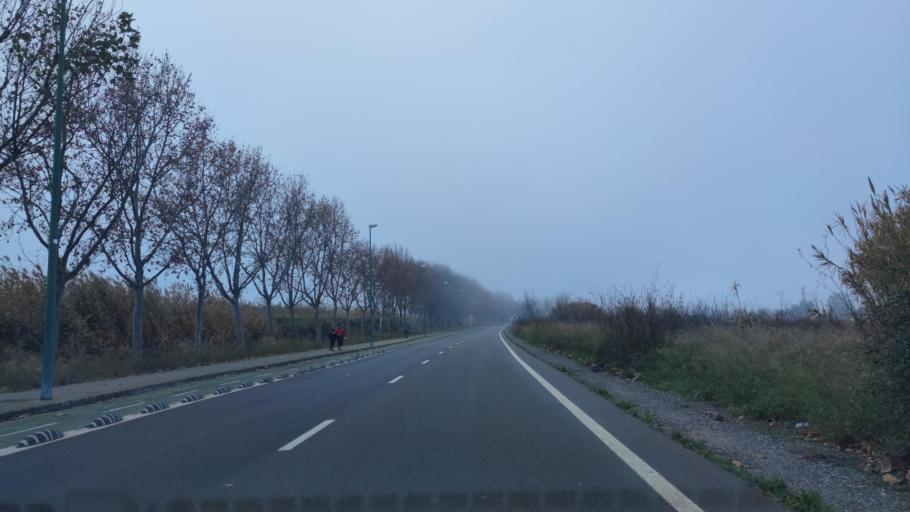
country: ES
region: Aragon
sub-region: Provincia de Zaragoza
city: Utebo
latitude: 41.7138
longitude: -1.0105
